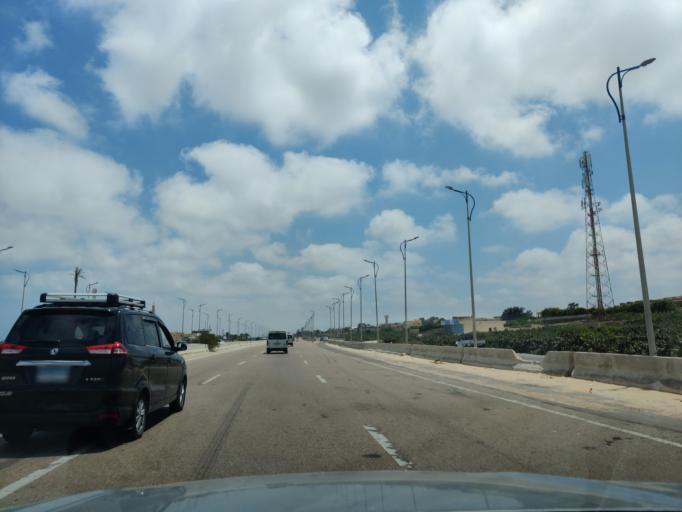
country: EG
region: Alexandria
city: Alexandria
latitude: 30.9663
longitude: 29.5547
